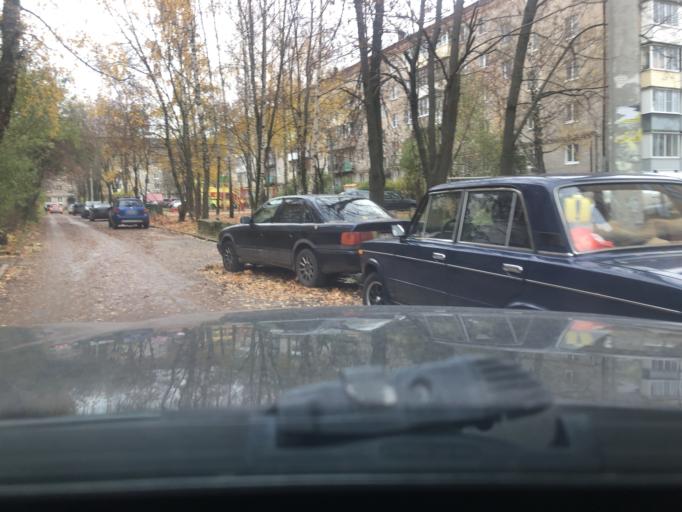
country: RU
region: Moskovskaya
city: Sergiyev Posad
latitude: 56.2968
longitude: 38.1168
